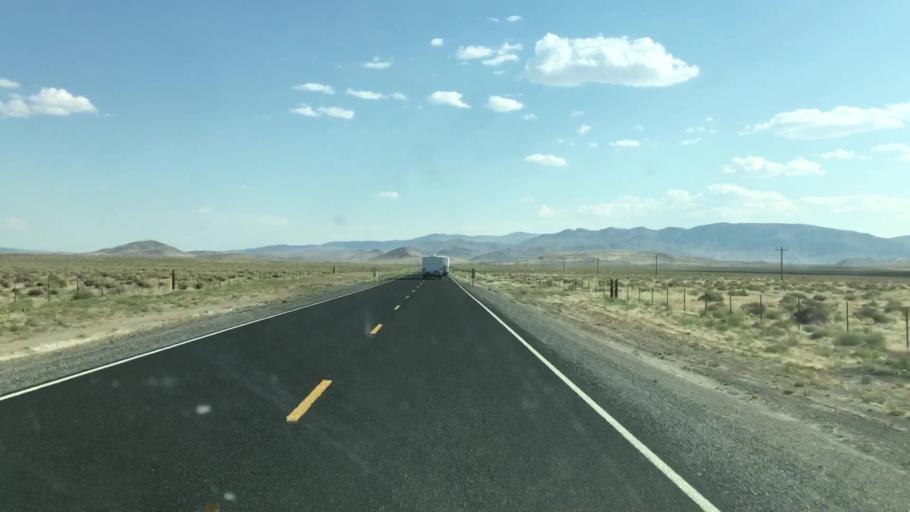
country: US
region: Nevada
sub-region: Lyon County
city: Fernley
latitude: 39.6730
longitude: -119.3327
